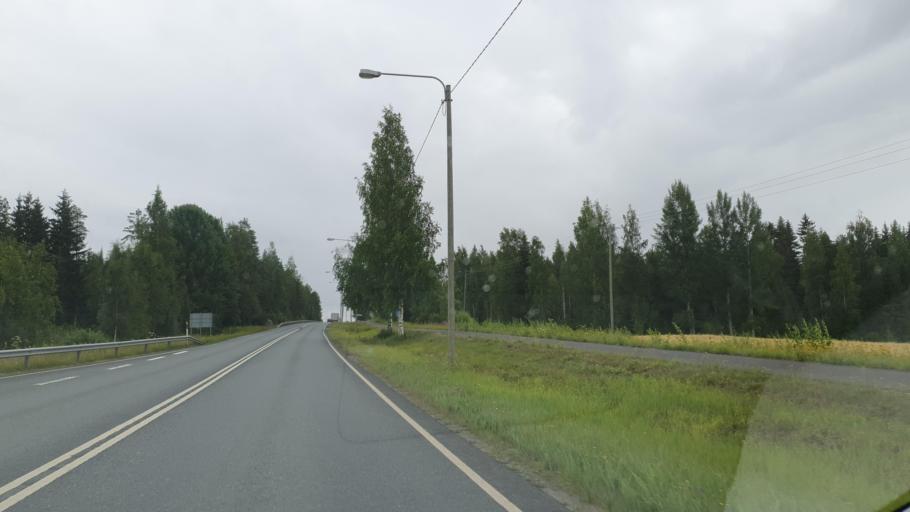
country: FI
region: Northern Savo
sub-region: Kuopio
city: Siilinjaervi
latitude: 63.1362
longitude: 27.6210
